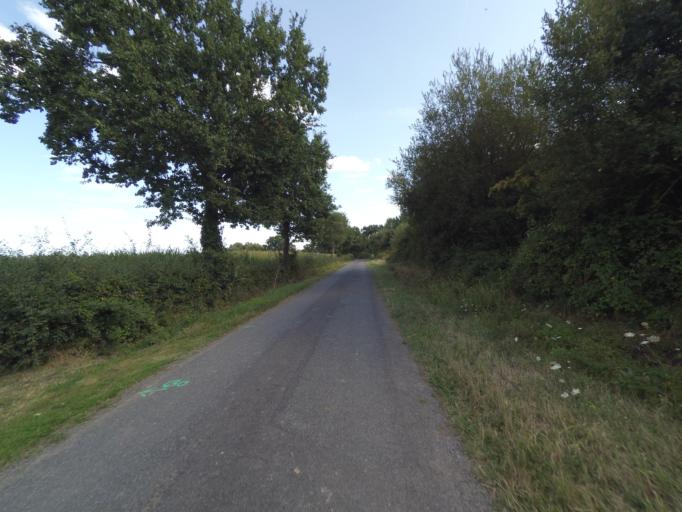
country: FR
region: Pays de la Loire
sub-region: Departement de la Loire-Atlantique
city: Vieillevigne
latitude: 46.9648
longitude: -1.4398
